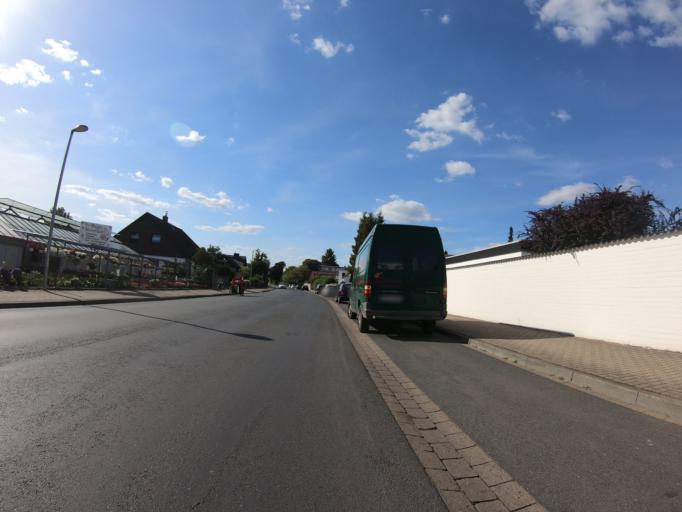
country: DE
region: Lower Saxony
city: Wolfenbuettel
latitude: 52.1748
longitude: 10.5370
